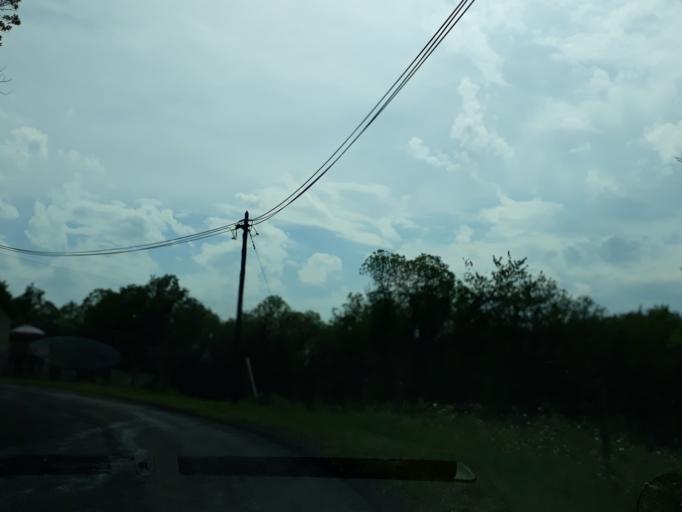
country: FR
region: Limousin
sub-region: Departement de la Correze
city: Beynat
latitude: 45.1176
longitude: 1.7604
